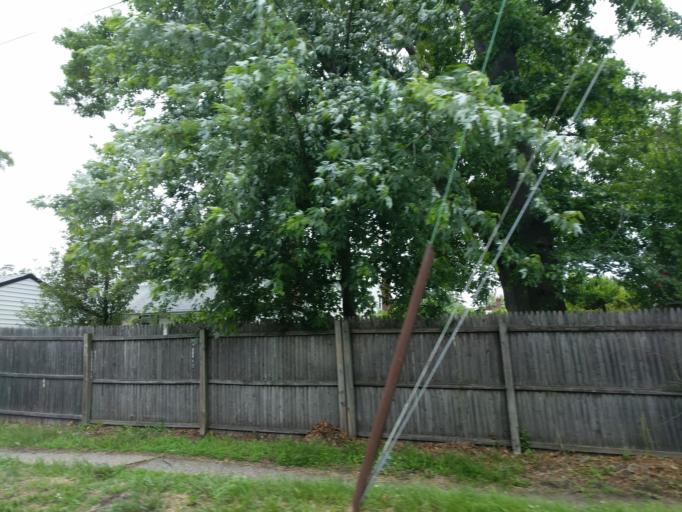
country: US
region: New York
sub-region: Nassau County
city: Woodmere
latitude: 40.6342
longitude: -73.7224
